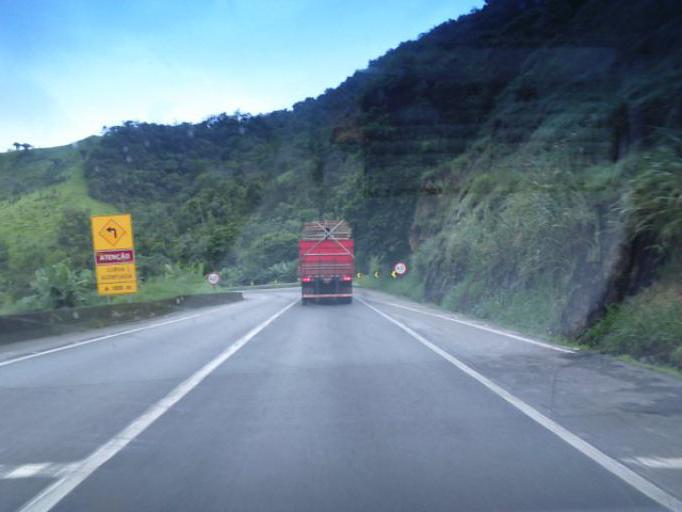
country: BR
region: Sao Paulo
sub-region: Cajati
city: Cajati
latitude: -24.8604
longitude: -48.2121
